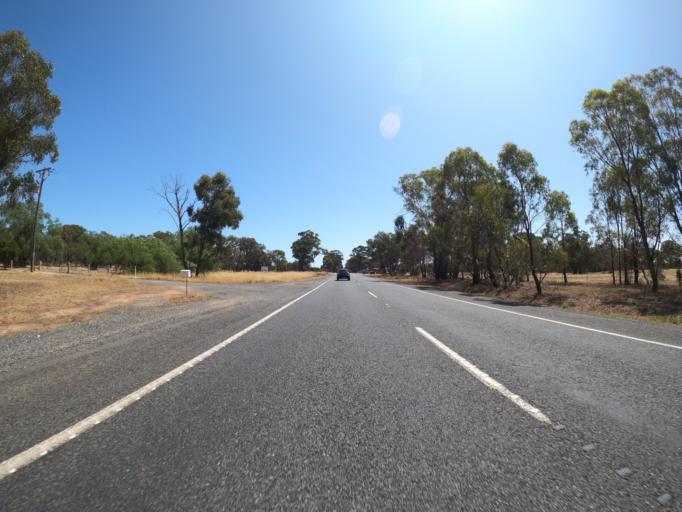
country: AU
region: New South Wales
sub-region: Corowa Shire
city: Corowa
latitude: -36.0610
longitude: 146.4114
